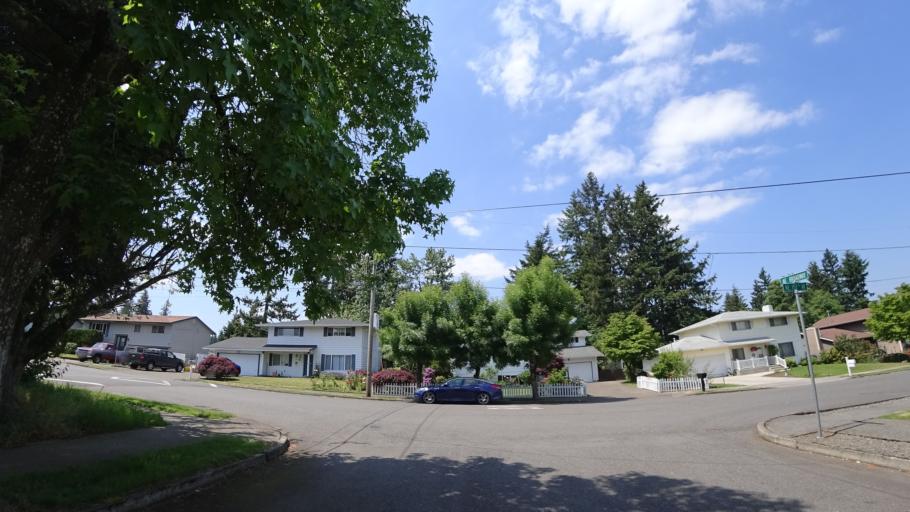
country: US
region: Oregon
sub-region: Multnomah County
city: Fairview
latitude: 45.5351
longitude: -122.5011
